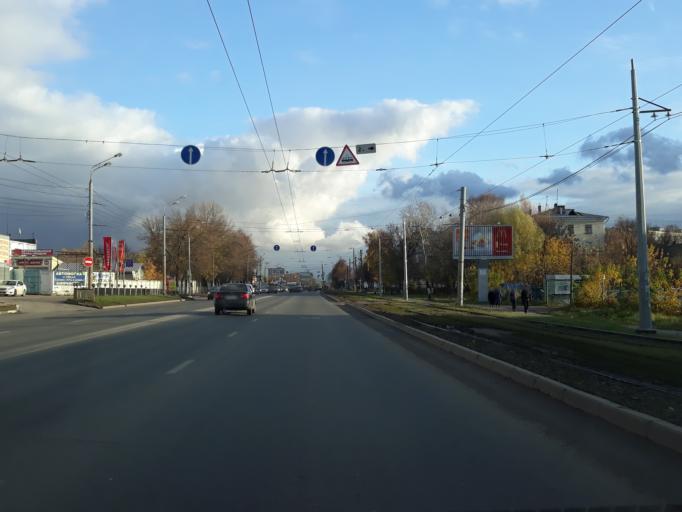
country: RU
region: Nizjnij Novgorod
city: Neklyudovo
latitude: 56.3432
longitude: 43.8753
